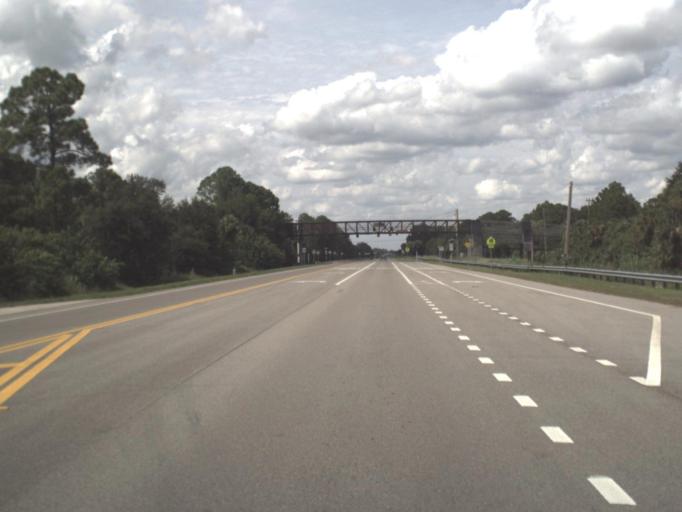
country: US
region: Florida
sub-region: Collier County
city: Immokalee
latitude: 26.4031
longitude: -81.3914
